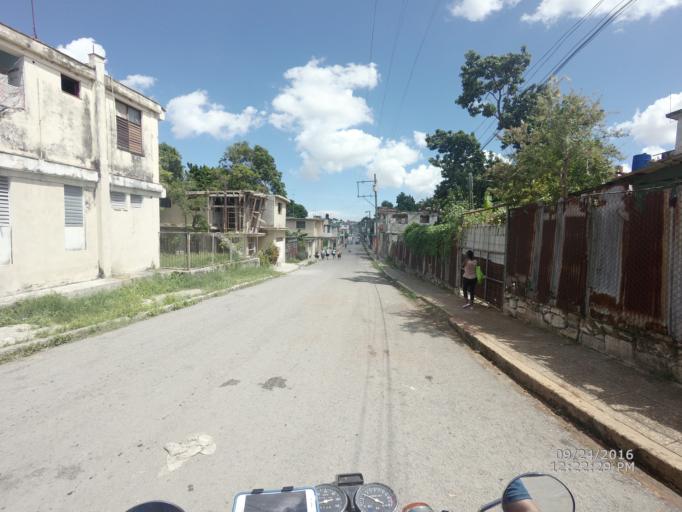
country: CU
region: La Habana
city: Diez de Octubre
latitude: 23.0966
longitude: -82.3544
